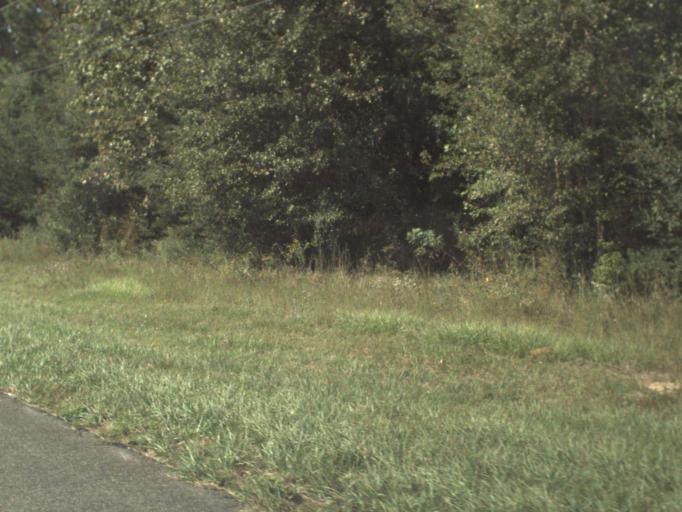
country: US
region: Alabama
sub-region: Geneva County
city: Geneva
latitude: 30.9410
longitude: -85.9504
